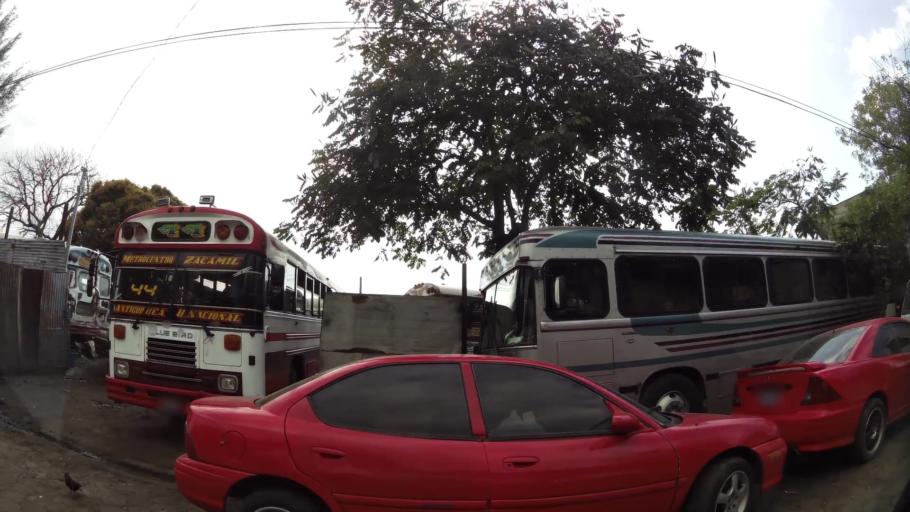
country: SV
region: San Salvador
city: Mejicanos
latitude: 13.7343
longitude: -89.2088
